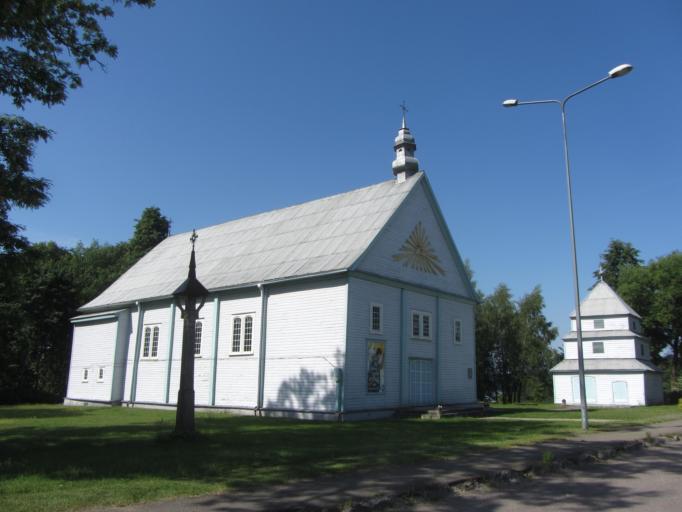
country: LT
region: Kauno apskritis
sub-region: Kauno rajonas
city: Karmelava
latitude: 54.8599
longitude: 24.2022
